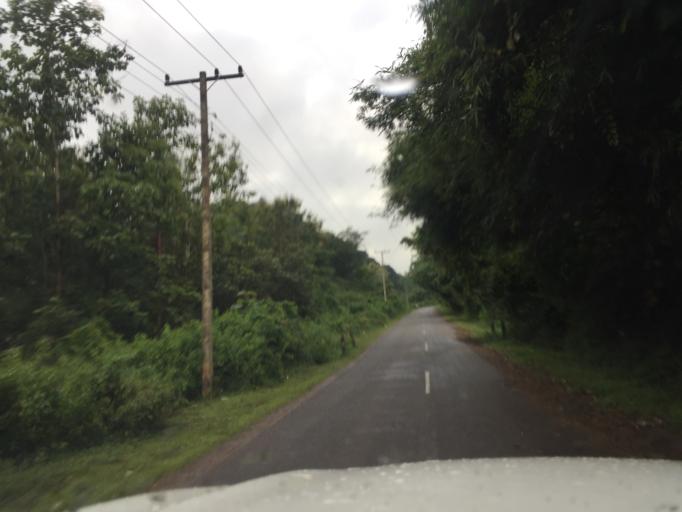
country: LA
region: Oudomxai
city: Muang La
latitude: 20.8664
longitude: 102.1297
